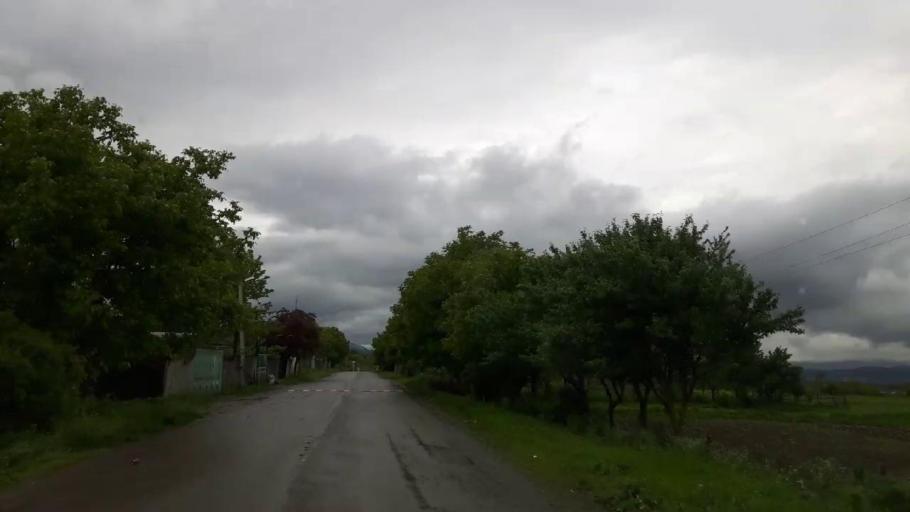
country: GE
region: Shida Kartli
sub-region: Khashuris Raioni
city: Khashuri
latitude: 41.9879
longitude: 43.6906
